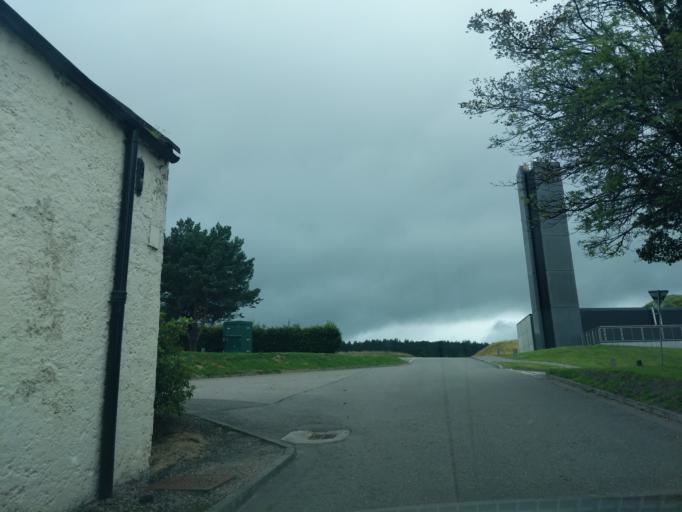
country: GB
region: Scotland
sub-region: Moray
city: Rothes
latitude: 57.4852
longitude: -3.2072
